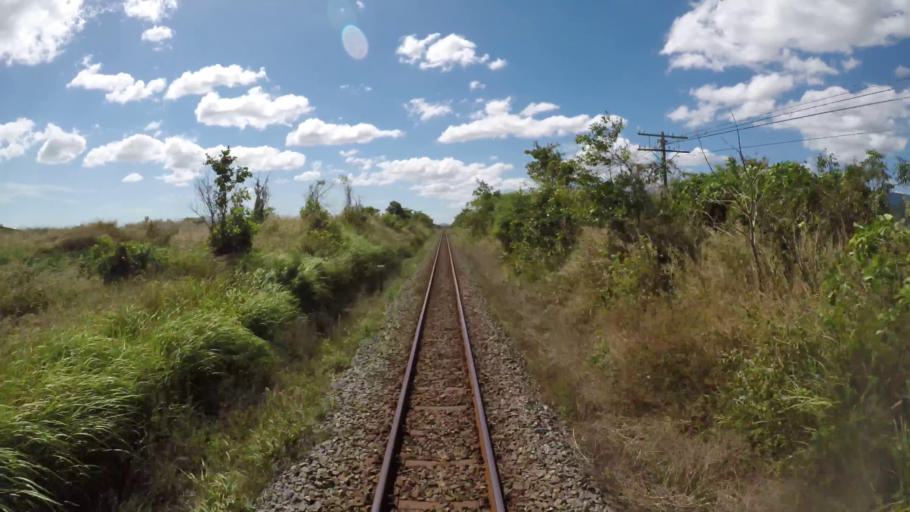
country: VN
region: Binh Thuan
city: Ma Lam
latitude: 11.0357
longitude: 108.0812
